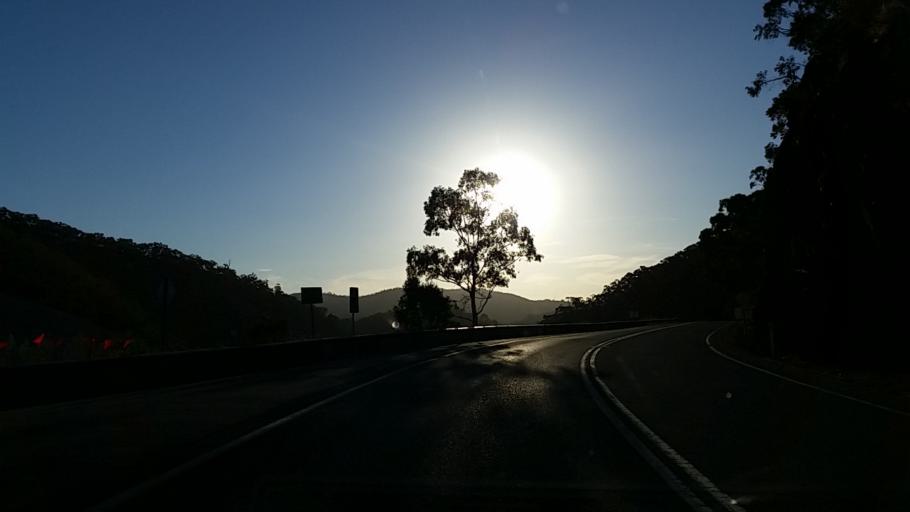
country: AU
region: South Australia
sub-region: Campbelltown
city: Athelstone
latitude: -34.8647
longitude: 138.7751
